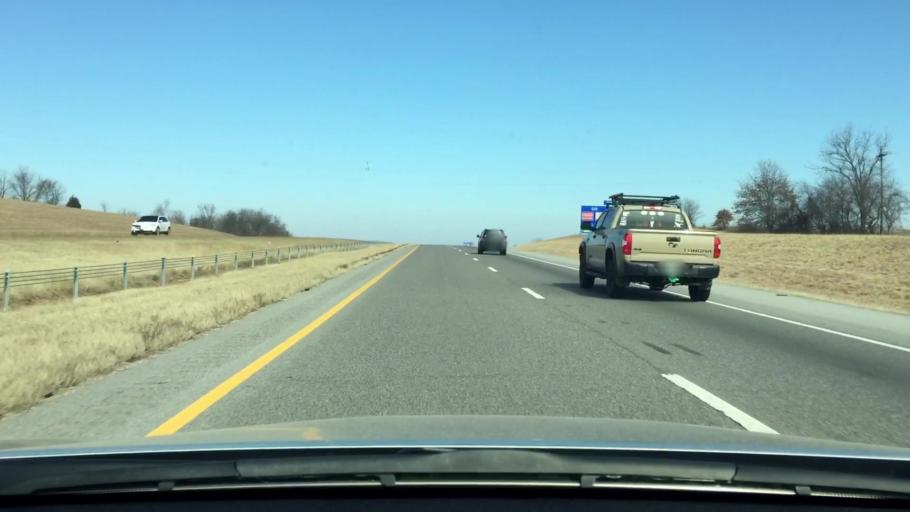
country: US
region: Oklahoma
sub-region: McClain County
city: Purcell
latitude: 34.9598
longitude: -97.3691
